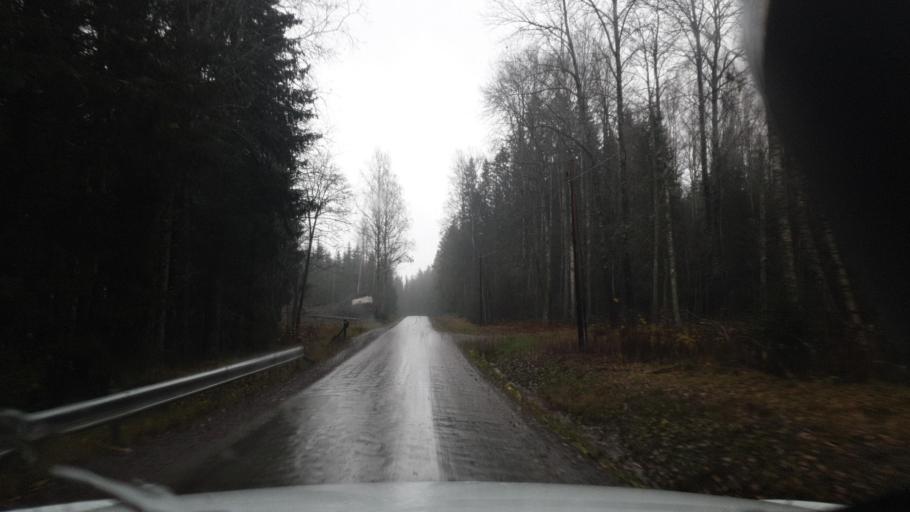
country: SE
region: Vaermland
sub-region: Karlstads Kommun
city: Edsvalla
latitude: 59.5046
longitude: 13.2007
